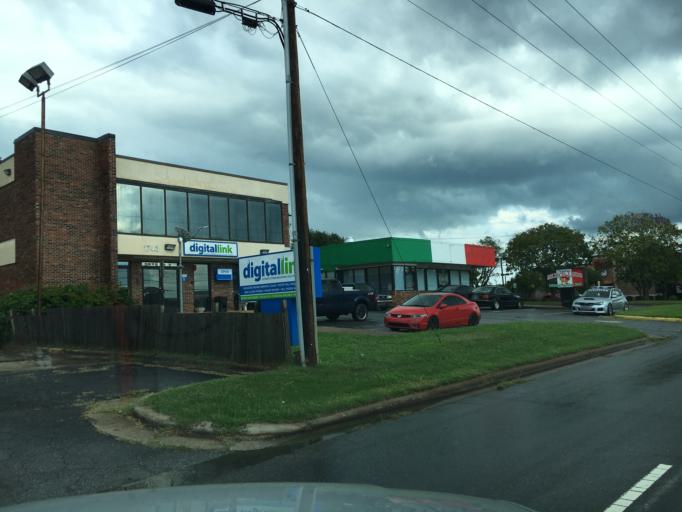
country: US
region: North Carolina
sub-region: Catawba County
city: Conover
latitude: 35.6992
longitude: -81.2618
